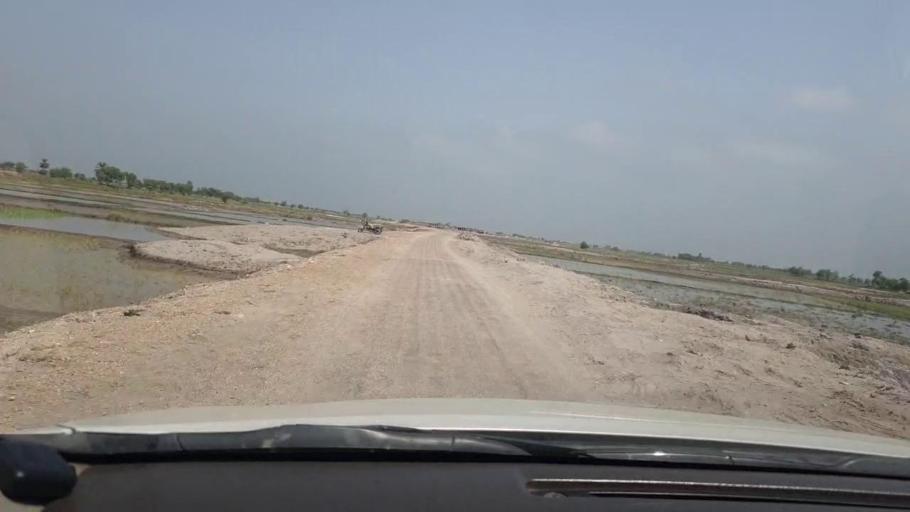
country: PK
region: Sindh
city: Shikarpur
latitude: 27.9975
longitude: 68.5610
